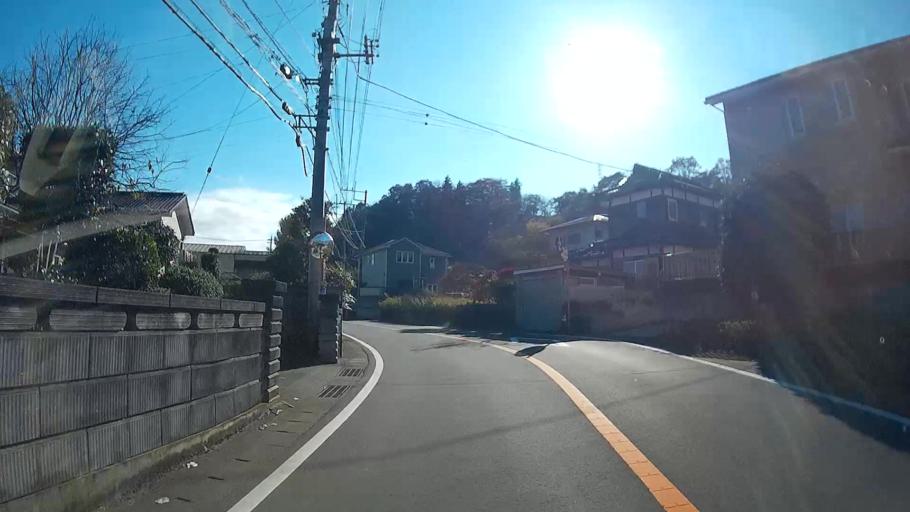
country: JP
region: Yamanashi
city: Uenohara
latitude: 35.6095
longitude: 139.1208
